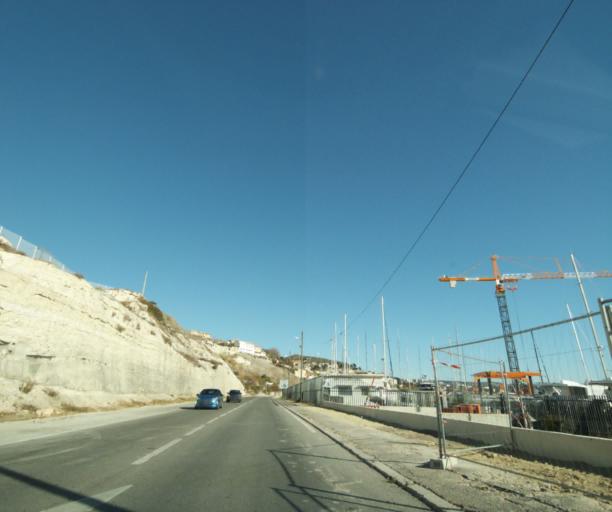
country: FR
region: Provence-Alpes-Cote d'Azur
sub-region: Departement des Bouches-du-Rhone
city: Marseille 16
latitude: 43.3609
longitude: 5.2999
